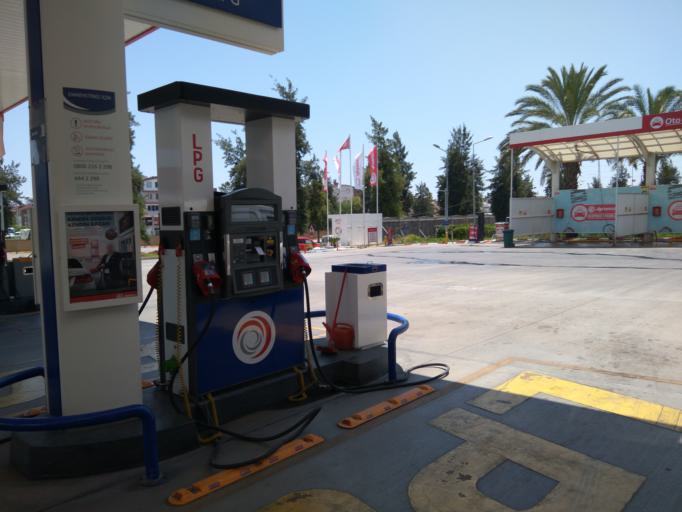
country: TR
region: Antalya
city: Antalya
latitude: 36.9190
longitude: 30.6665
